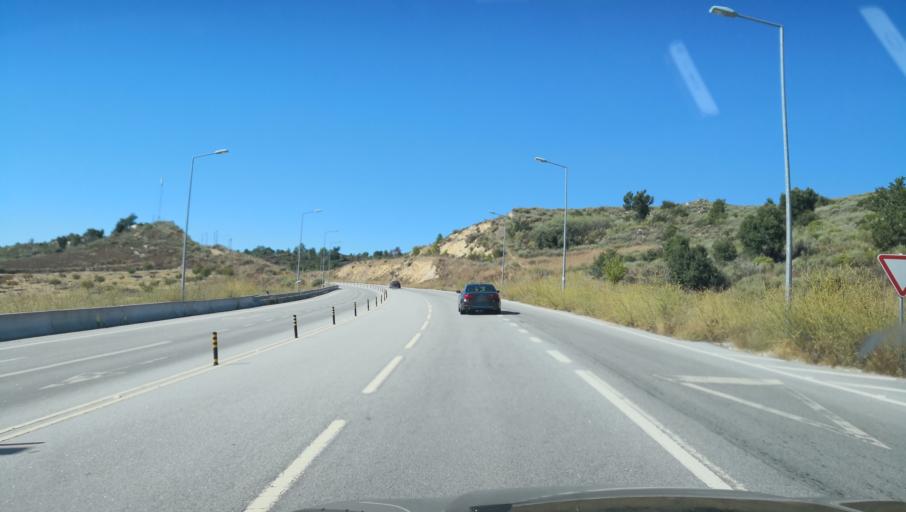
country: PT
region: Vila Real
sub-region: Valpacos
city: Valpacos
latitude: 41.5658
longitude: -7.2714
